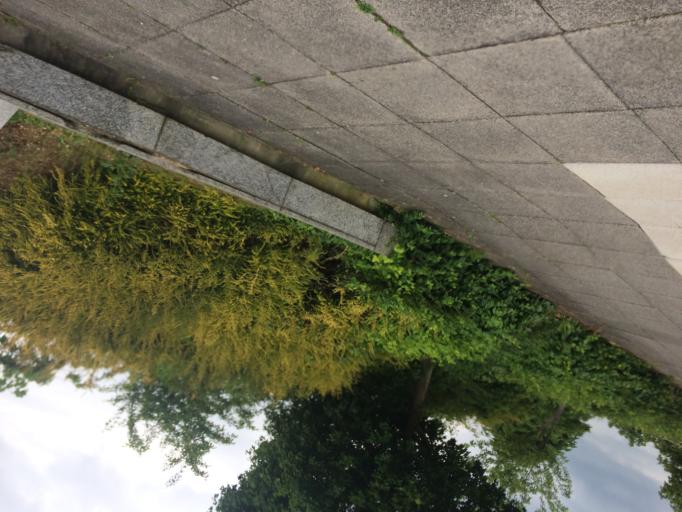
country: GB
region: England
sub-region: Milton Keynes
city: Milton Keynes
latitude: 52.0431
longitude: -0.7475
